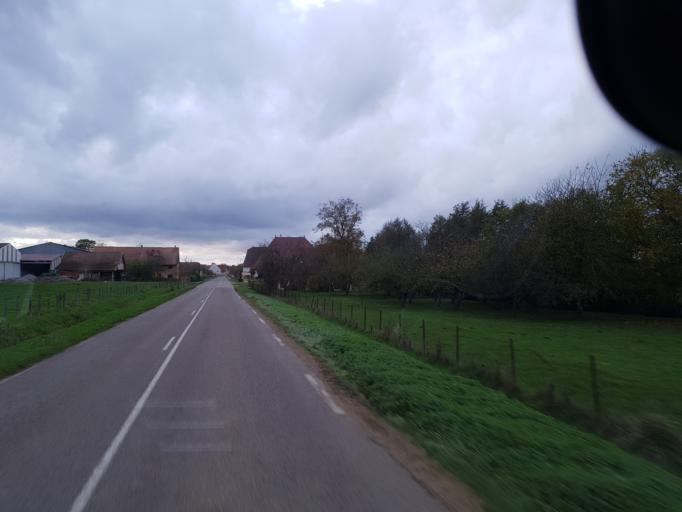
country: FR
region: Franche-Comte
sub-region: Departement du Jura
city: Mont-sous-Vaudrey
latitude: 46.9382
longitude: 5.6657
